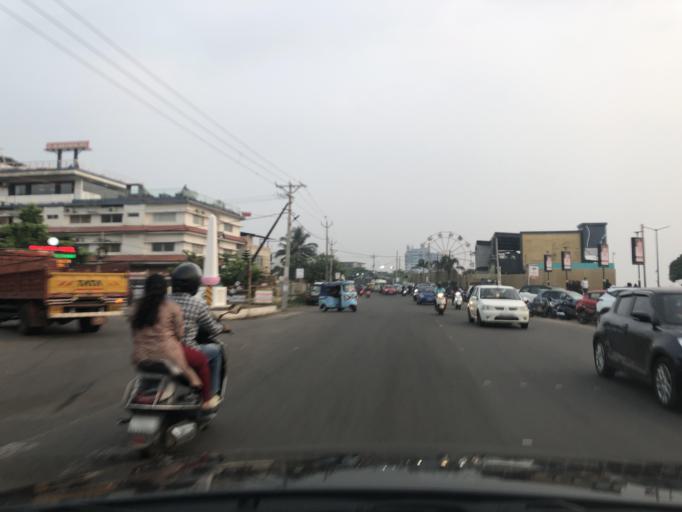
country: IN
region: Kerala
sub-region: Kozhikode
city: Kozhikode
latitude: 11.2515
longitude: 75.7713
